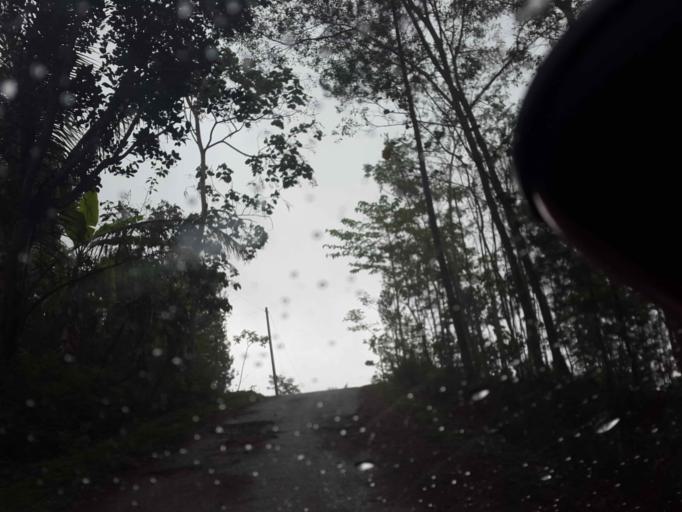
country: ID
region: East Java
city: Krajan Mrayan
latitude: -8.1087
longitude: 111.3407
